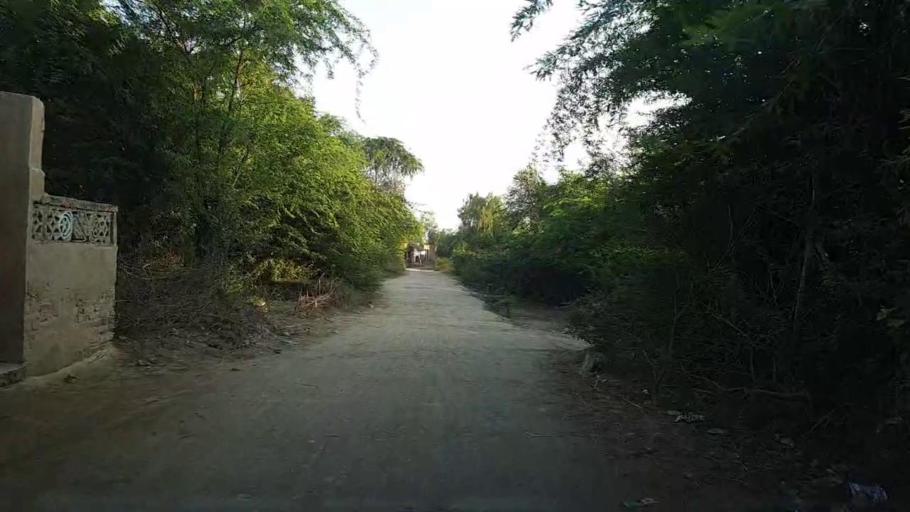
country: PK
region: Sindh
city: Kario
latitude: 24.6898
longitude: 68.6731
